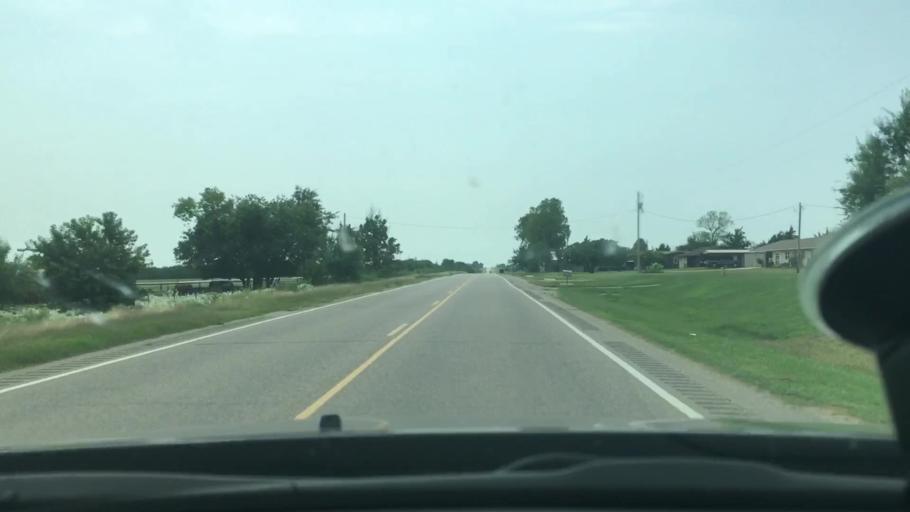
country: US
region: Oklahoma
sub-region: Marshall County
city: Madill
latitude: 34.0481
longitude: -96.7611
